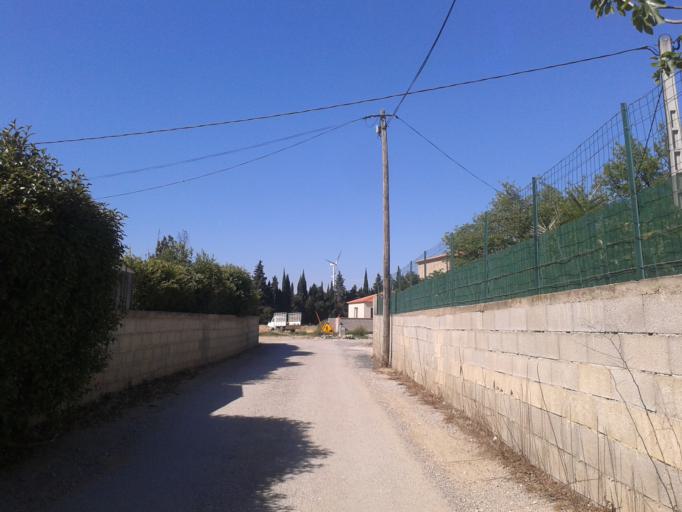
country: FR
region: Languedoc-Roussillon
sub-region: Departement des Pyrenees-Orientales
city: Pezilla-la-Riviere
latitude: 42.7006
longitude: 2.7777
